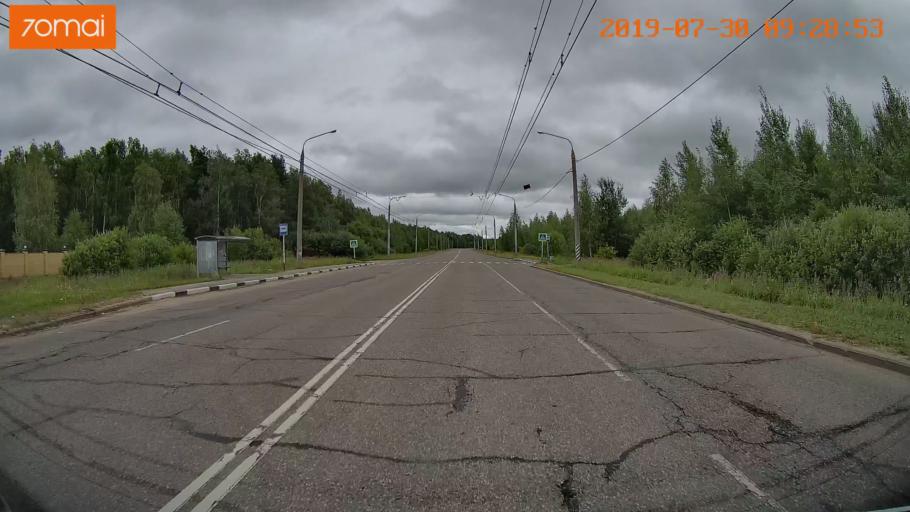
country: RU
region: Ivanovo
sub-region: Gorod Ivanovo
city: Ivanovo
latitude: 56.9496
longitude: 40.9473
